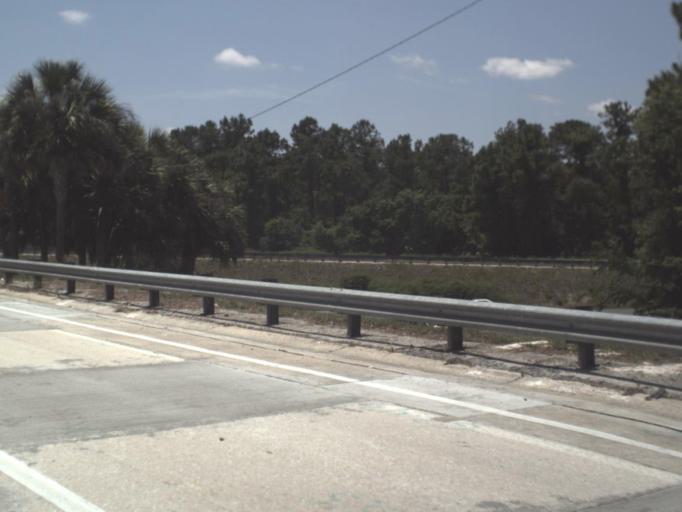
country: US
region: Florida
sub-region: Saint Johns County
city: Fruit Cove
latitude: 30.1858
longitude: -81.5581
